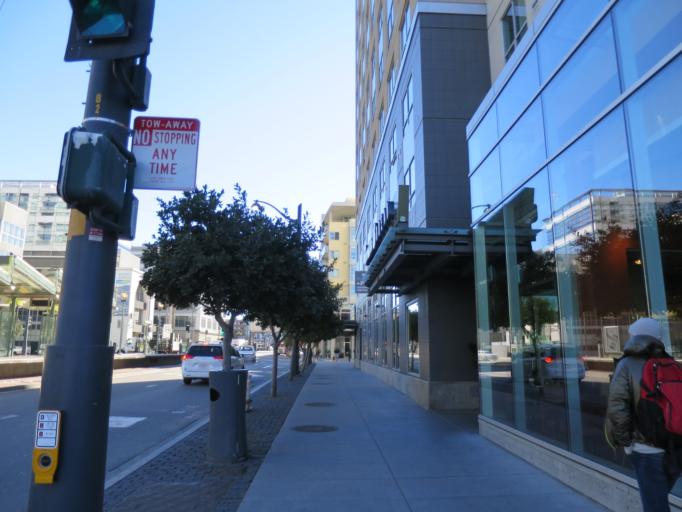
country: US
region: California
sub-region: San Francisco County
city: San Francisco
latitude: 37.7759
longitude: -122.3937
